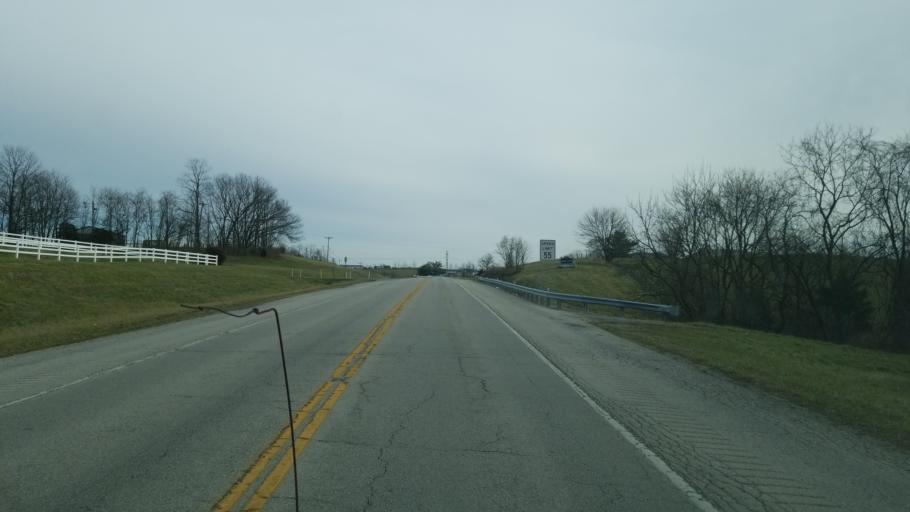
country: US
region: Kentucky
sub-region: Robertson County
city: Mount Olivet
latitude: 38.4782
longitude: -83.8929
